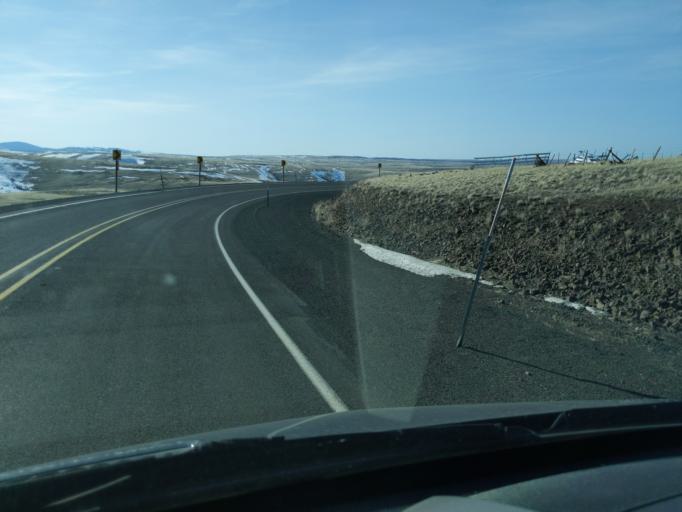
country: US
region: Oregon
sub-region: Umatilla County
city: Pilot Rock
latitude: 45.2994
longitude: -119.0048
